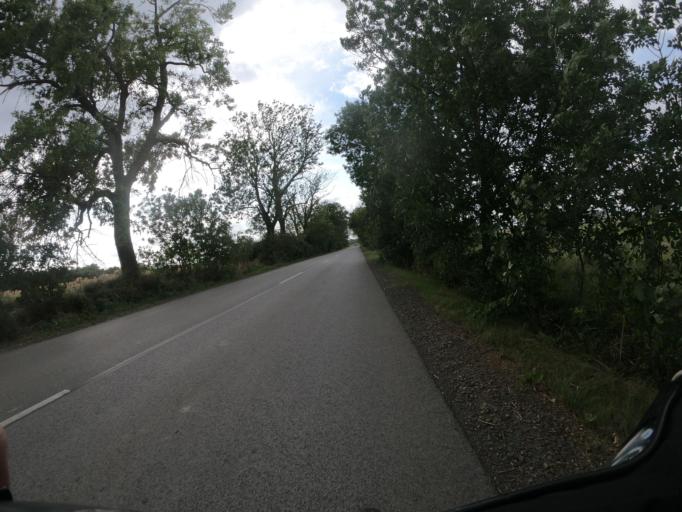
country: HU
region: Borsod-Abauj-Zemplen
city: Mezocsat
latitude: 47.8218
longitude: 20.8530
